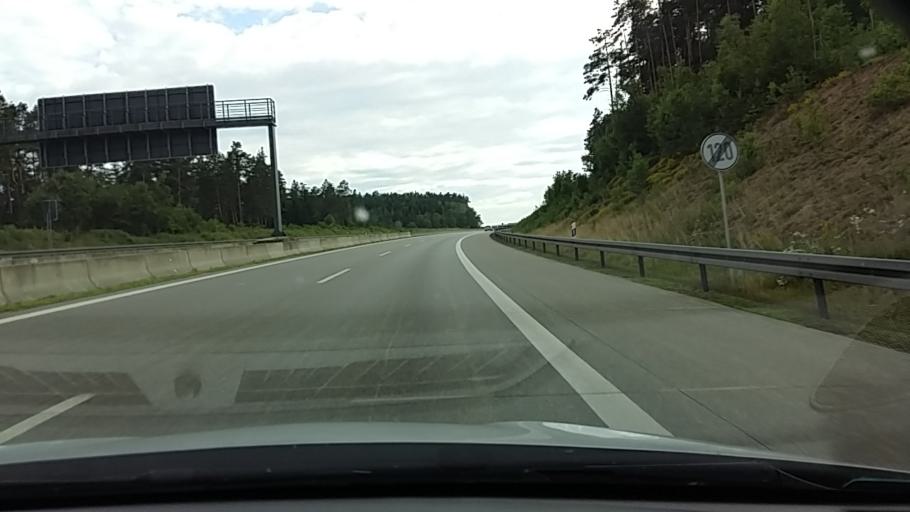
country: DE
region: Bavaria
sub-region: Upper Palatinate
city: Pfreimd
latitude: 49.5062
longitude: 12.1587
